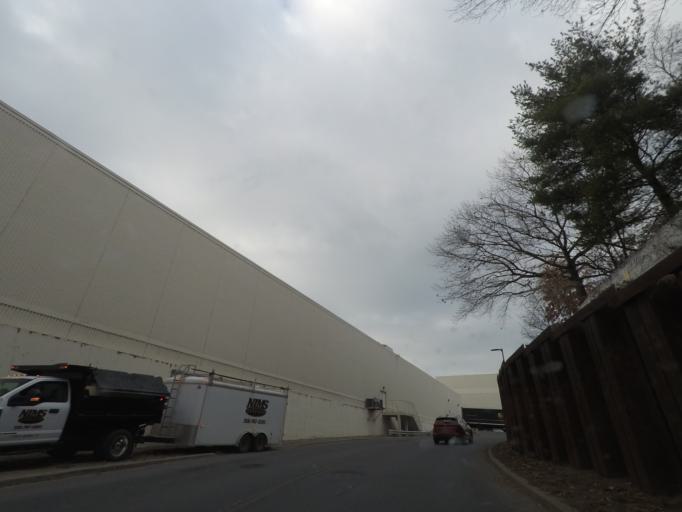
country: US
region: New York
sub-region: Albany County
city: McKownville
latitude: 42.6903
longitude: -73.8510
